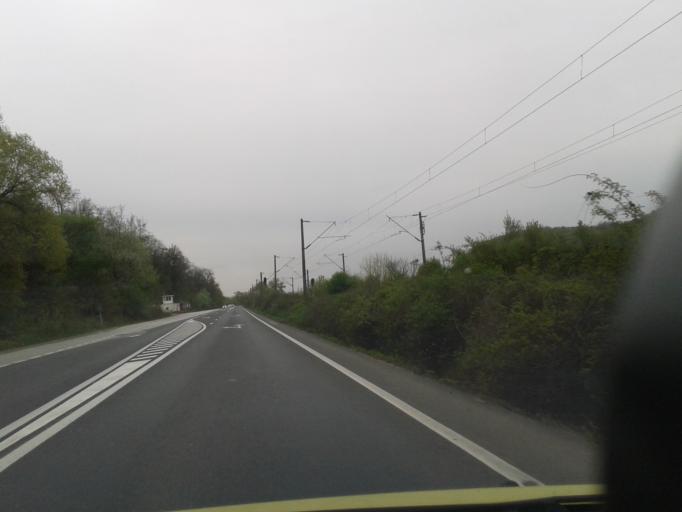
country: RO
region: Arad
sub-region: Oras Lipova
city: Lipova
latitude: 46.1074
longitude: 21.7384
